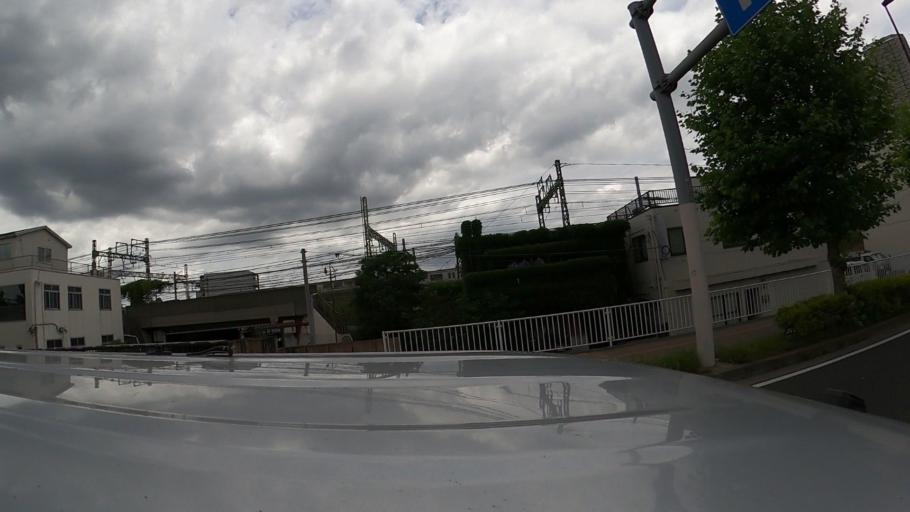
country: JP
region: Kanagawa
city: Yokohama
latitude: 35.4850
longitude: 139.6499
